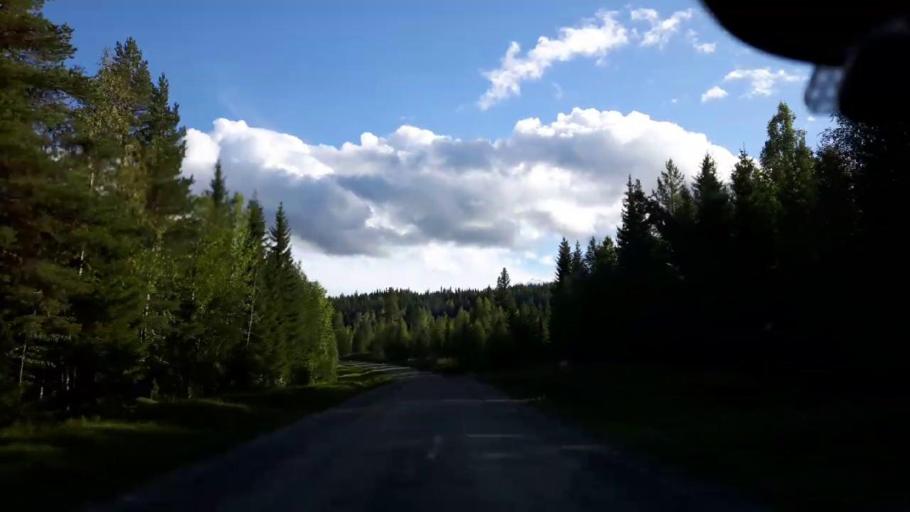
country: SE
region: Jaemtland
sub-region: Stroemsunds Kommun
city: Stroemsund
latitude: 63.3575
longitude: 15.5686
